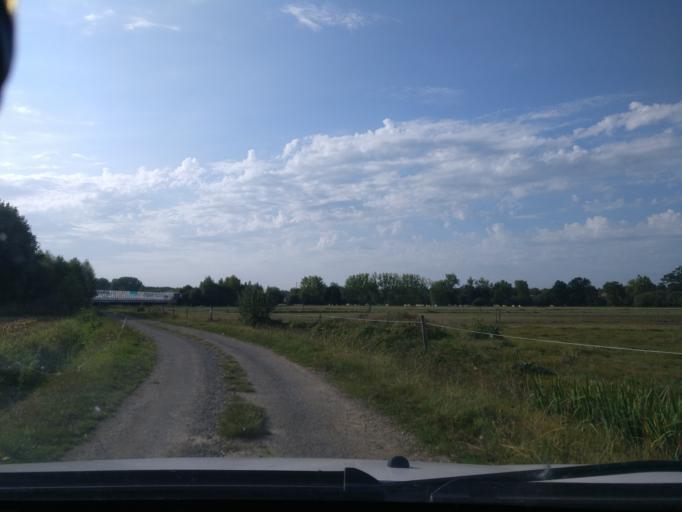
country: FR
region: Brittany
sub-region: Departement d'Ille-et-Vilaine
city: Fouillard
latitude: 48.1357
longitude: -1.5738
